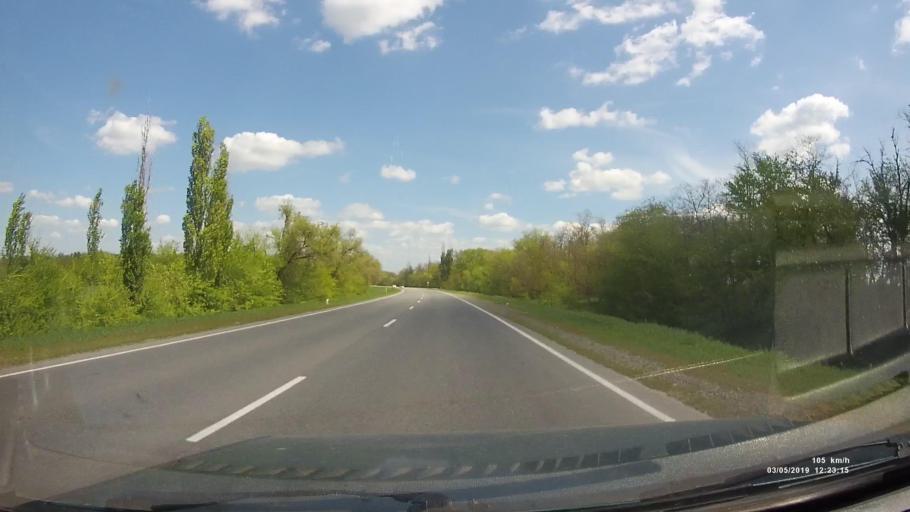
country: RU
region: Rostov
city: Semikarakorsk
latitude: 47.4078
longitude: 40.6795
